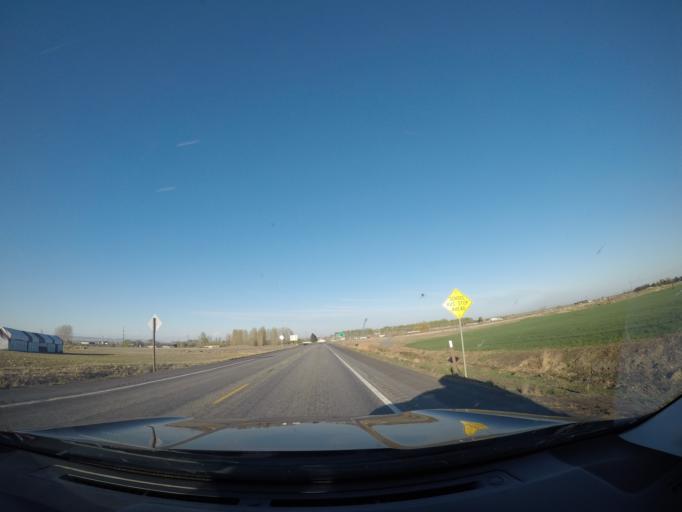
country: US
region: Washington
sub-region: Grant County
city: Quincy
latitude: 47.0907
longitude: -119.8604
